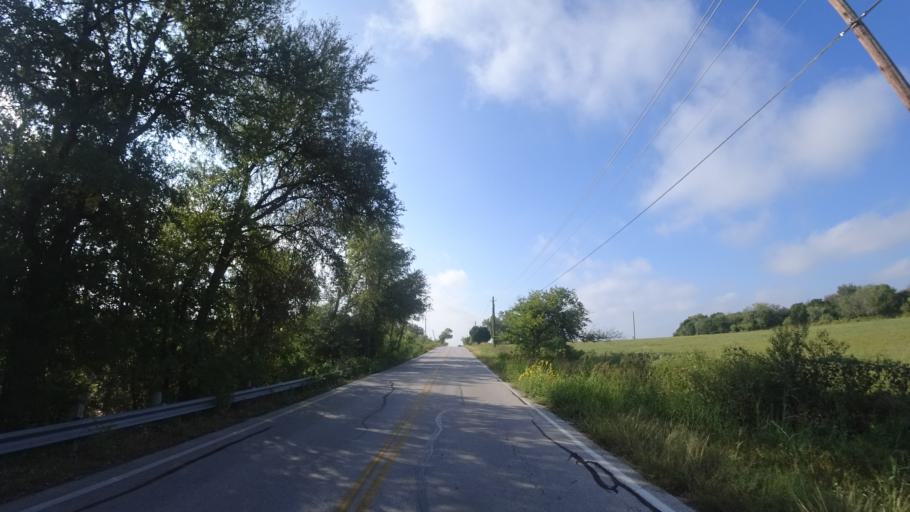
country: US
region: Texas
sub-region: Travis County
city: Manor
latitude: 30.3477
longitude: -97.6463
